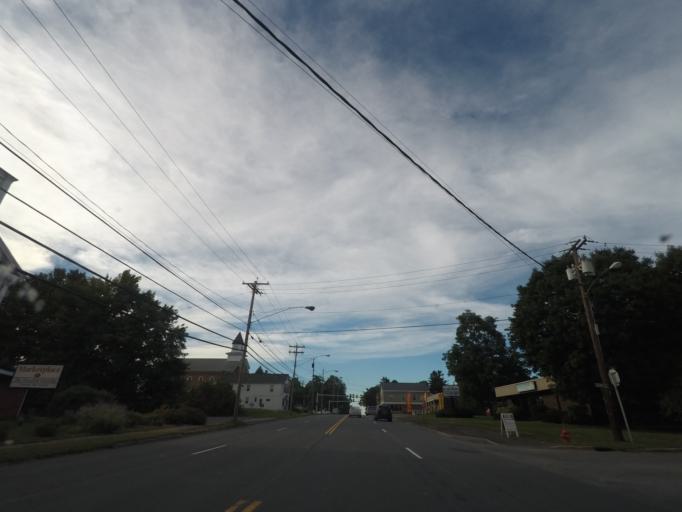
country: US
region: New York
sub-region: Rensselaer County
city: East Greenbush
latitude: 42.5879
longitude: -73.6986
